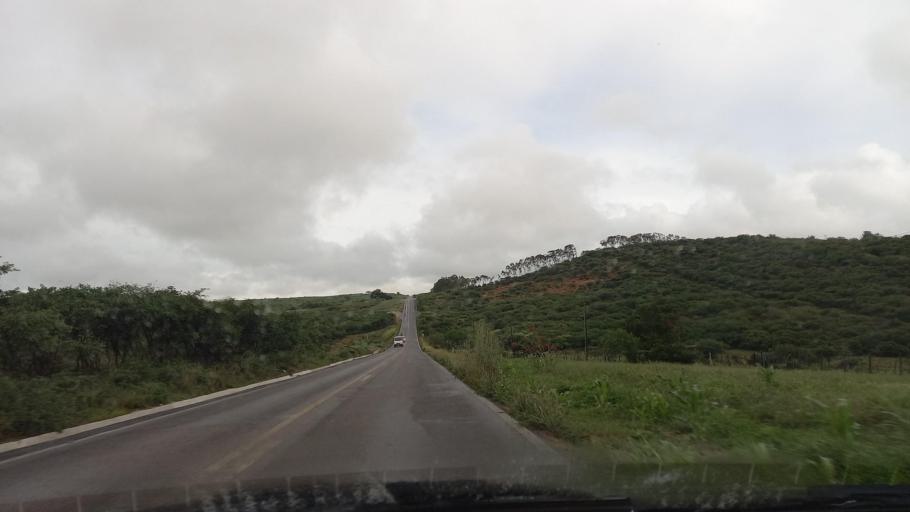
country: BR
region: Pernambuco
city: Garanhuns
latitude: -8.8438
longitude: -36.5277
